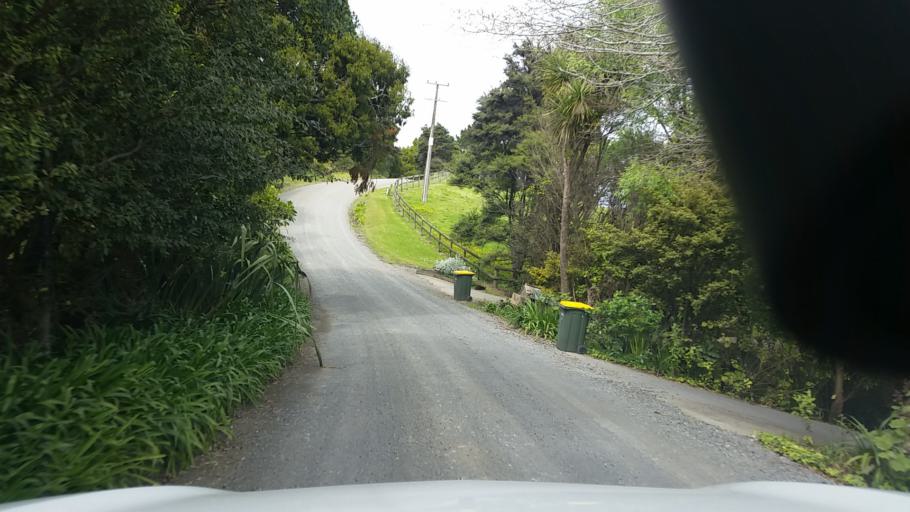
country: NZ
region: Auckland
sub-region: Auckland
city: Muriwai Beach
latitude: -36.8442
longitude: 174.5111
